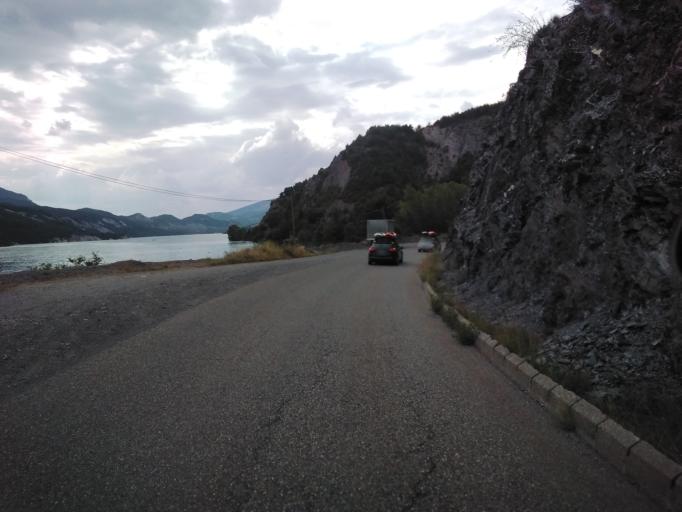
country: FR
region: Provence-Alpes-Cote d'Azur
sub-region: Departement des Alpes-de-Haute-Provence
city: Seyne-les-Alpes
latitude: 44.4619
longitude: 6.3705
